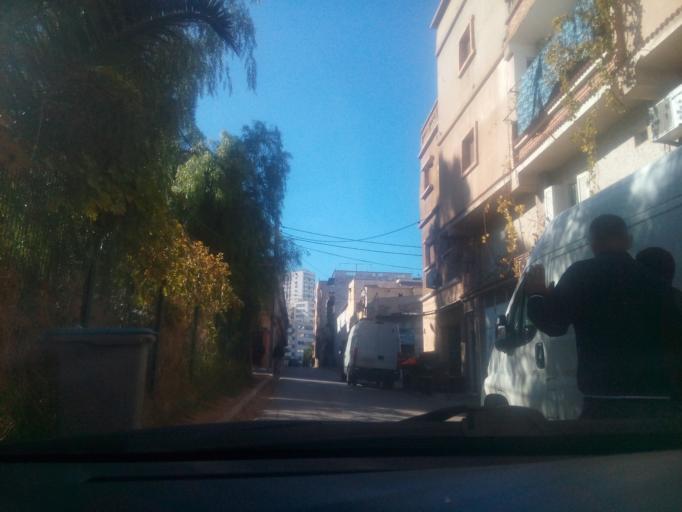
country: DZ
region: Oran
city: Oran
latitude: 35.7032
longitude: -0.6252
